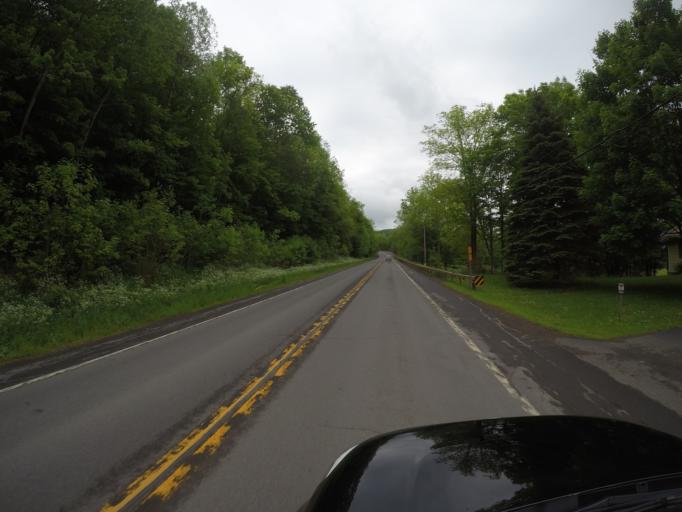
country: US
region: New York
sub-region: Delaware County
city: Delhi
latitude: 42.2600
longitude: -74.9210
